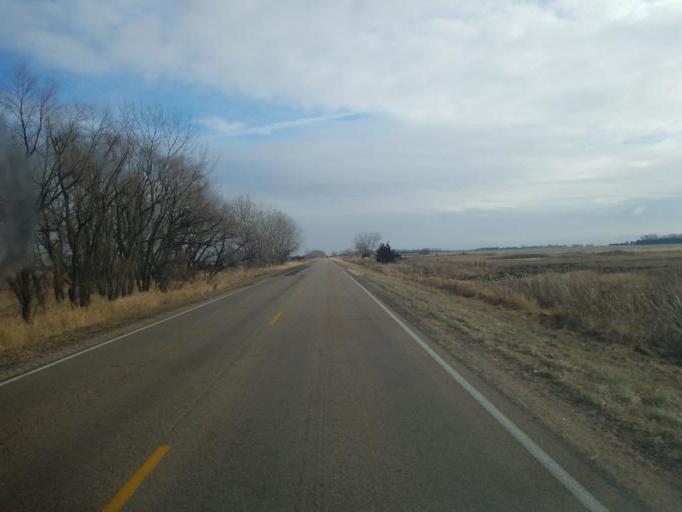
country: US
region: Nebraska
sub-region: Pierce County
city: Pierce
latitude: 42.2303
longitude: -97.5869
